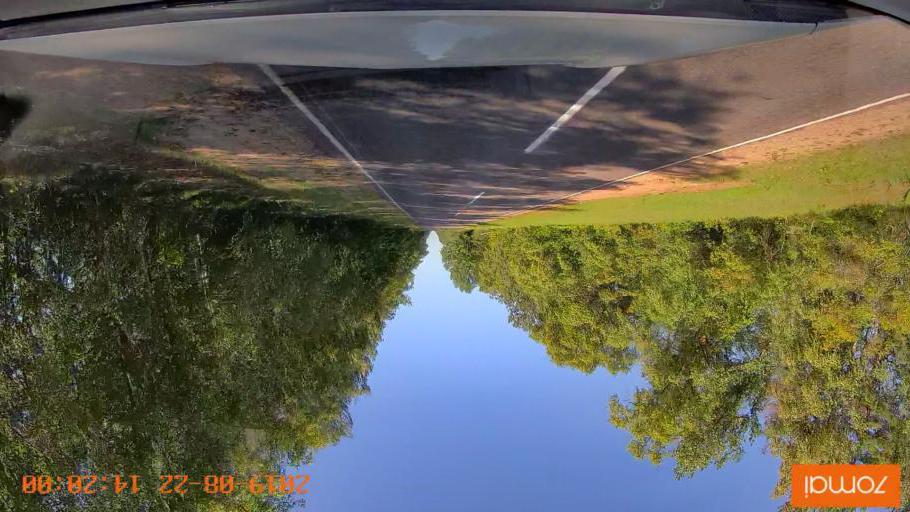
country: BY
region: Mogilev
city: Asipovichy
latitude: 53.2638
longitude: 28.5150
